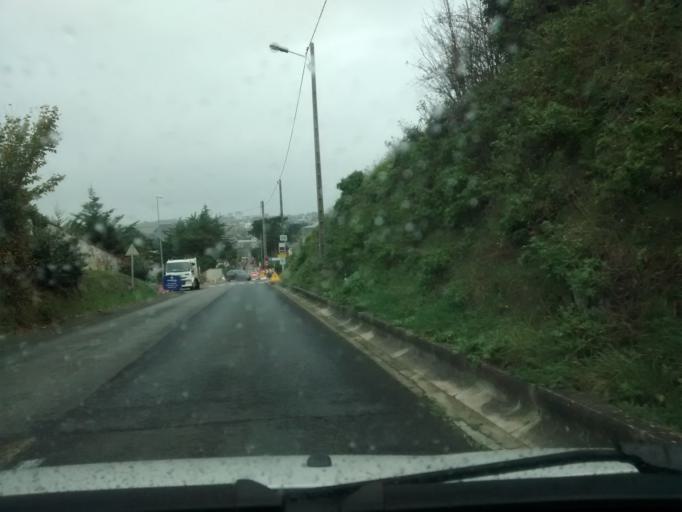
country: FR
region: Lower Normandy
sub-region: Departement de la Manche
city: Saint-Pair-sur-Mer
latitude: 48.8080
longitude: -1.5704
